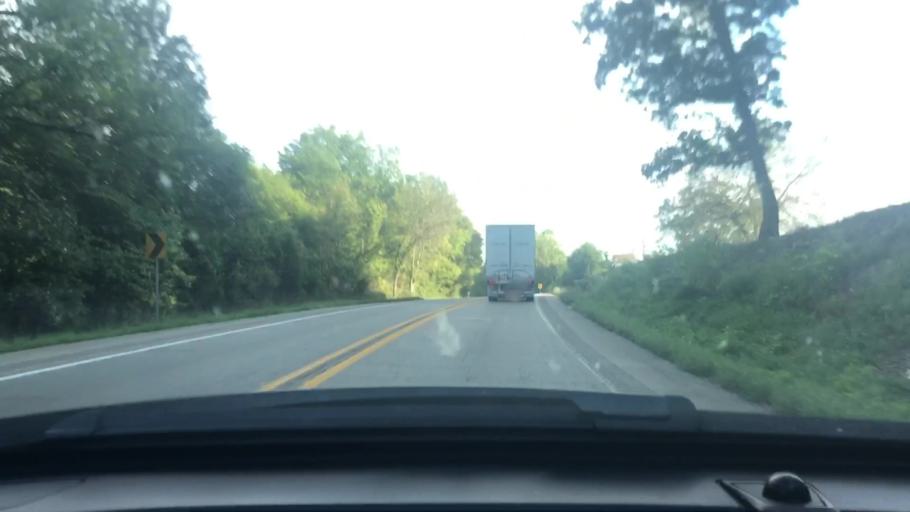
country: US
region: Arkansas
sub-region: Randolph County
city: Pocahontas
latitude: 36.2156
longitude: -91.2150
